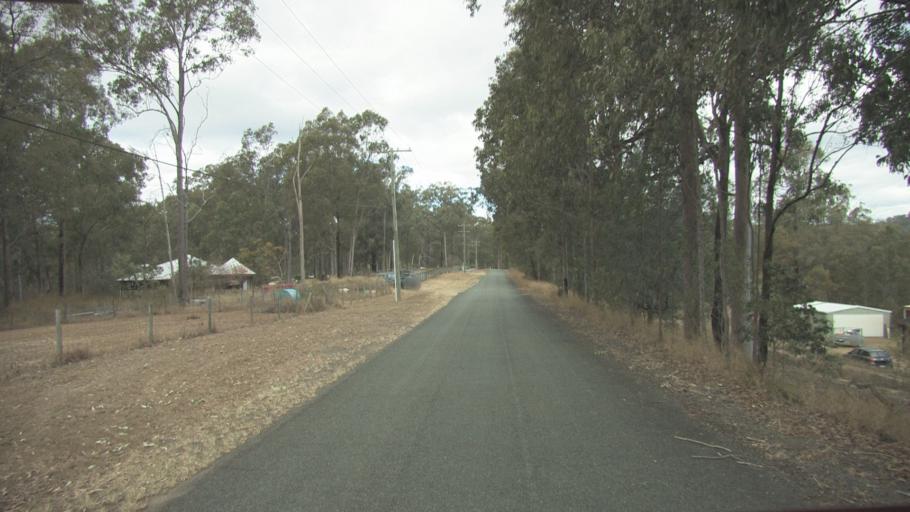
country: AU
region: Queensland
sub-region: Logan
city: Cedar Vale
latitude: -27.8813
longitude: 153.0356
